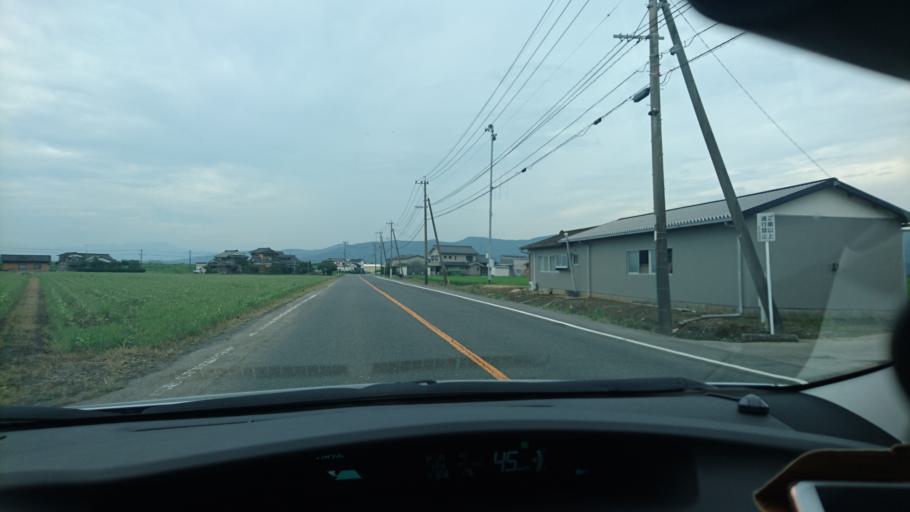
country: JP
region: Saga Prefecture
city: Takeocho-takeo
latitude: 33.2033
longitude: 130.1202
